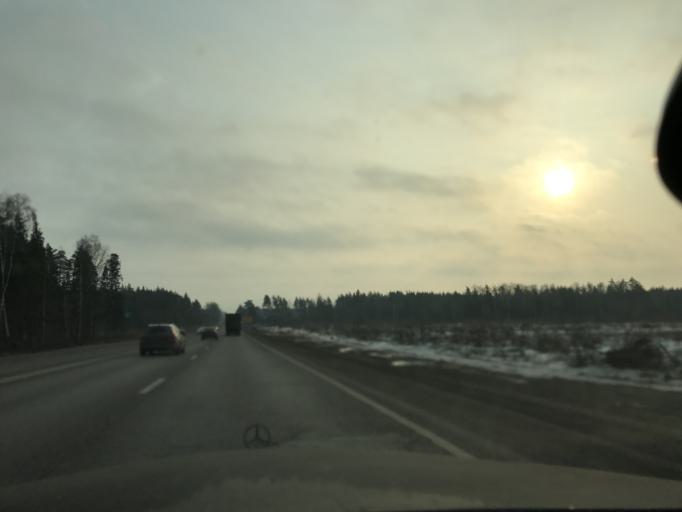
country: RU
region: Vladimir
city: Pokrov
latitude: 55.9270
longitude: 39.3059
